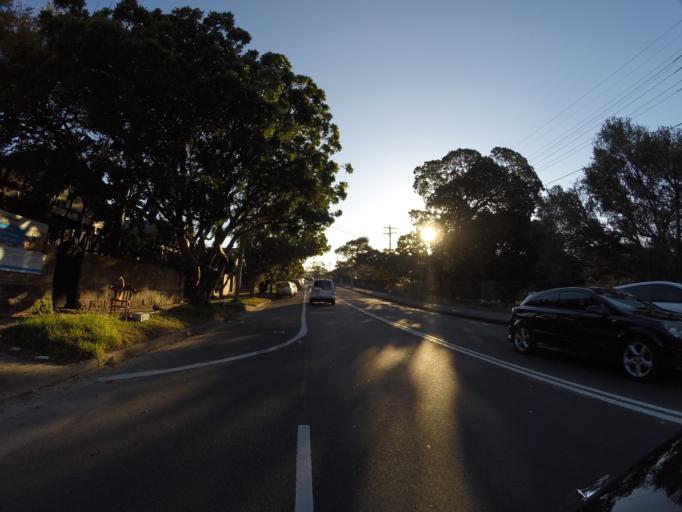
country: AU
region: New South Wales
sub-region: Waverley
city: Bondi Junction
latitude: -33.9028
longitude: 151.2447
